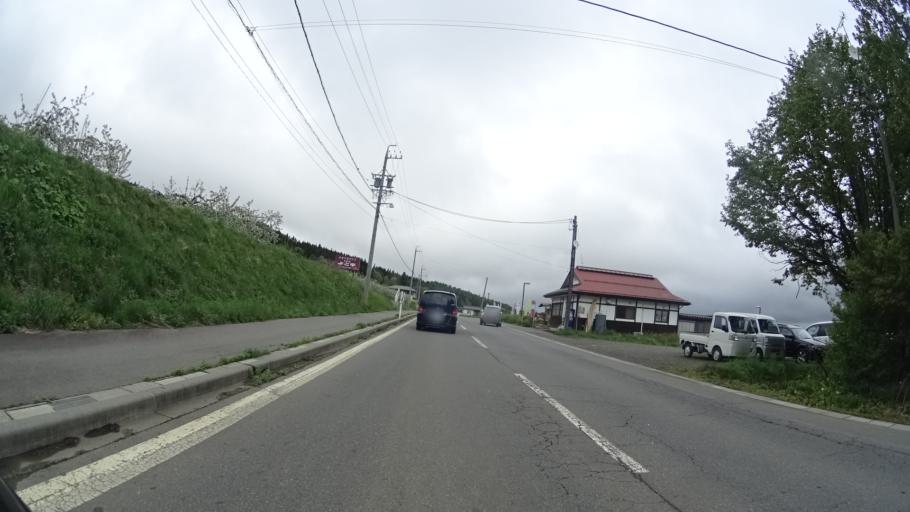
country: JP
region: Nagano
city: Nagano-shi
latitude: 36.7426
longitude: 138.2055
